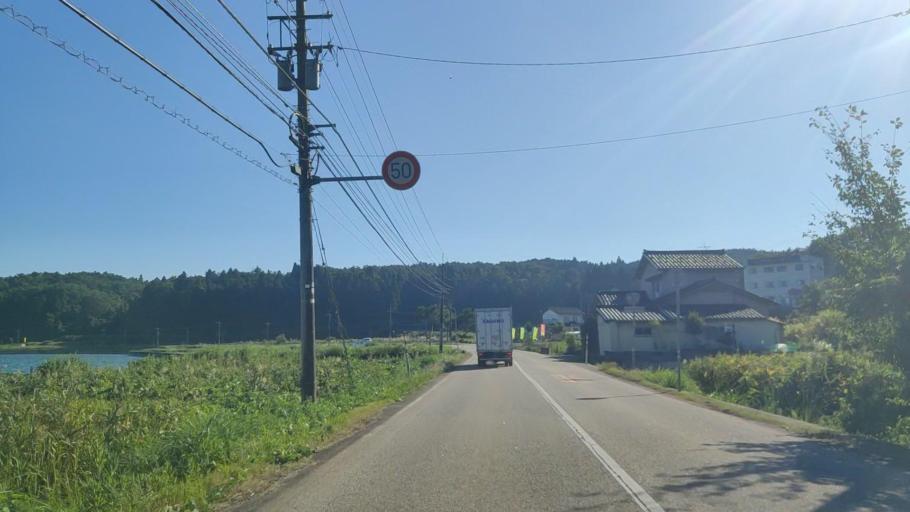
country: JP
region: Ishikawa
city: Nanao
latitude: 37.2038
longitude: 136.9067
